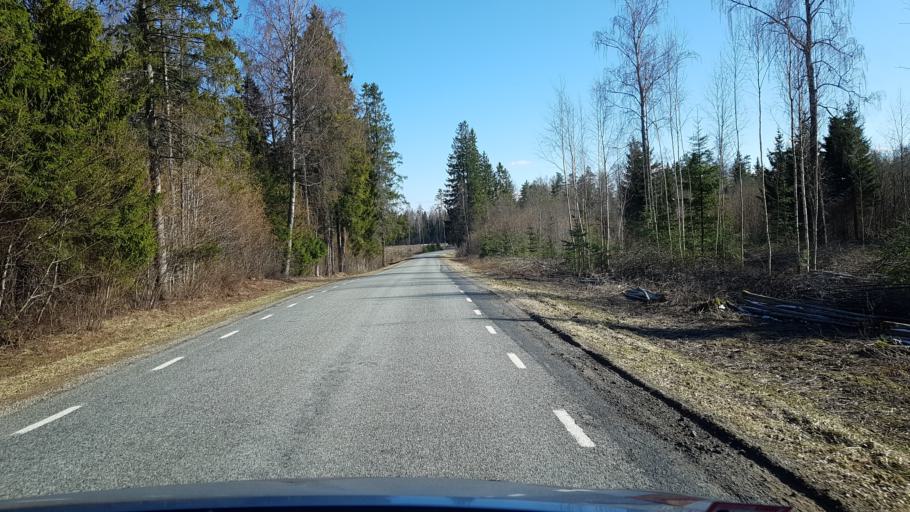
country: EE
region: Laeaene-Virumaa
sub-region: Kadrina vald
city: Kadrina
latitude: 59.3913
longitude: 26.0195
